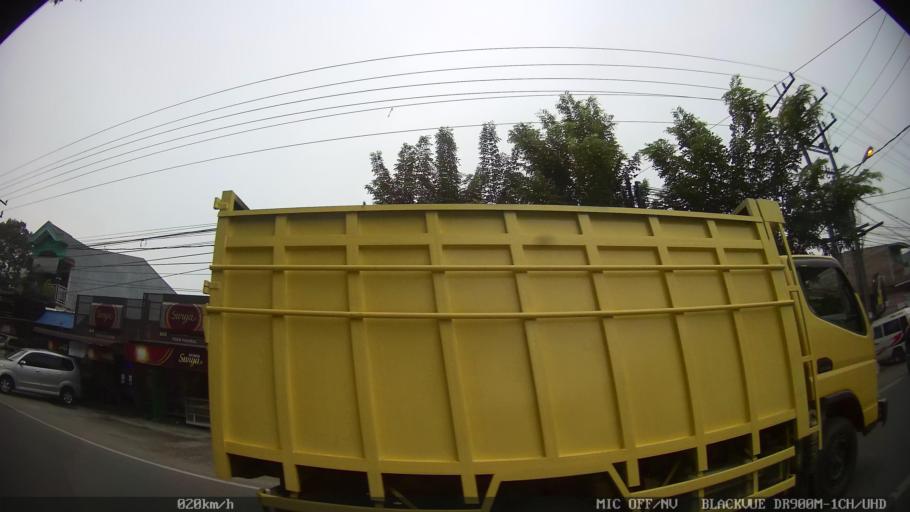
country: ID
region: North Sumatra
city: Deli Tua
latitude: 3.5414
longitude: 98.7178
